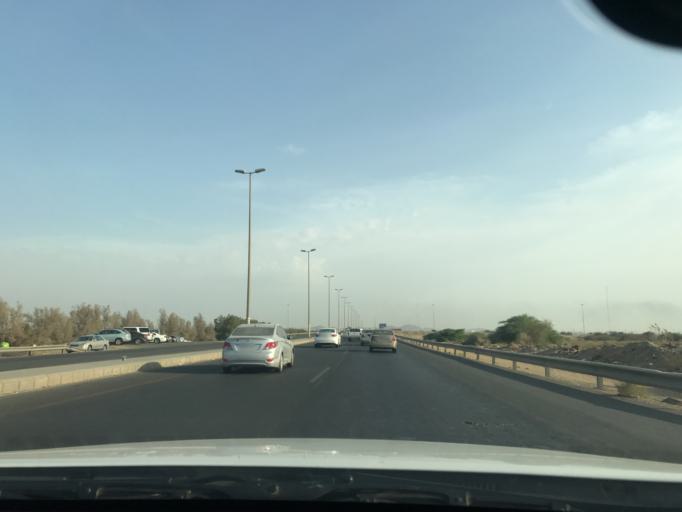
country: SA
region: Makkah
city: Jeddah
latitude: 21.3947
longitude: 39.4268
